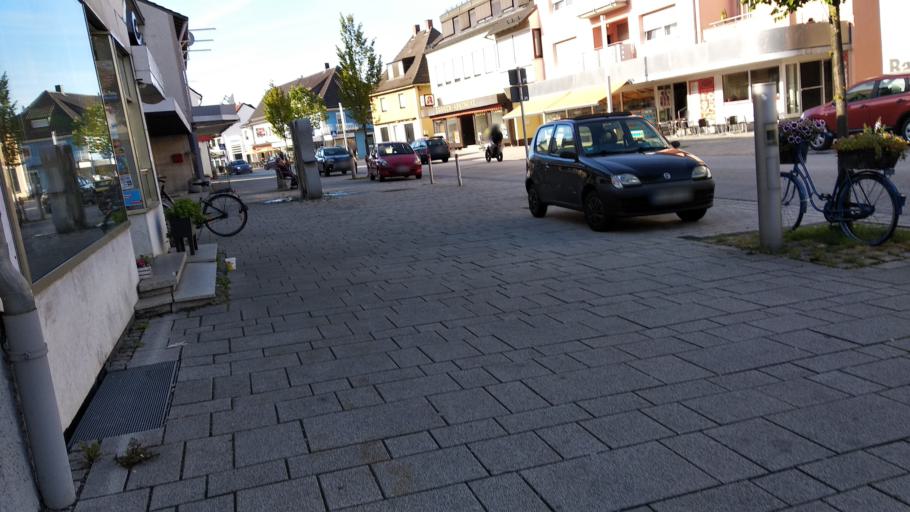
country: DE
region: Bavaria
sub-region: Swabia
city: Vohringen
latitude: 48.2778
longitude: 10.0787
